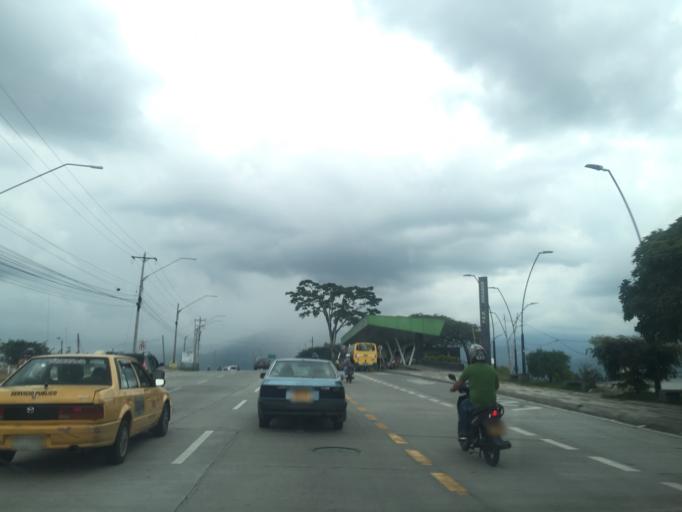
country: CO
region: Quindio
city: Armenia
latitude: 4.5219
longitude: -75.6854
